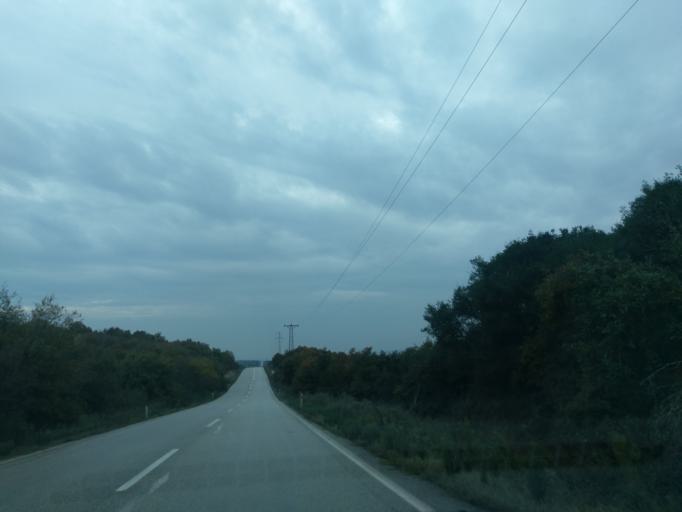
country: TR
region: Istanbul
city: Canta
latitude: 41.1566
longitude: 28.1068
